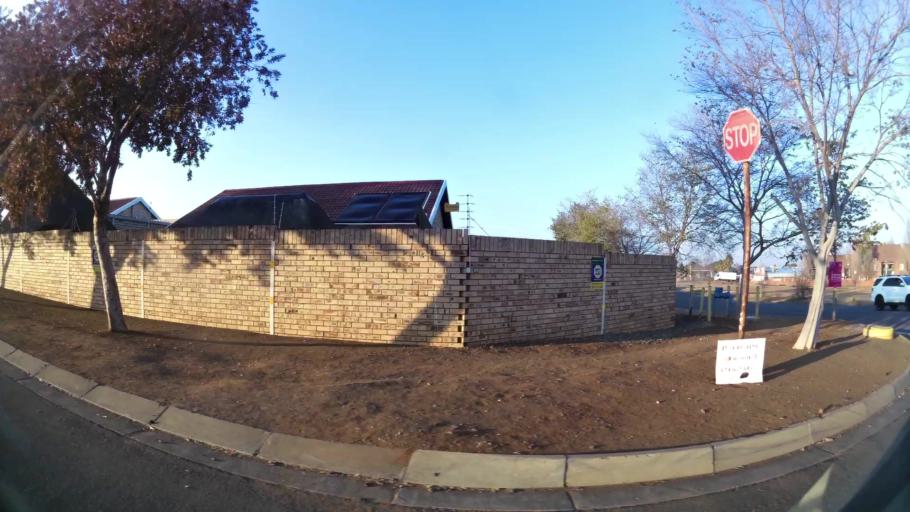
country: ZA
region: Orange Free State
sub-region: Mangaung Metropolitan Municipality
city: Bloemfontein
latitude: -29.0925
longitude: 26.1649
